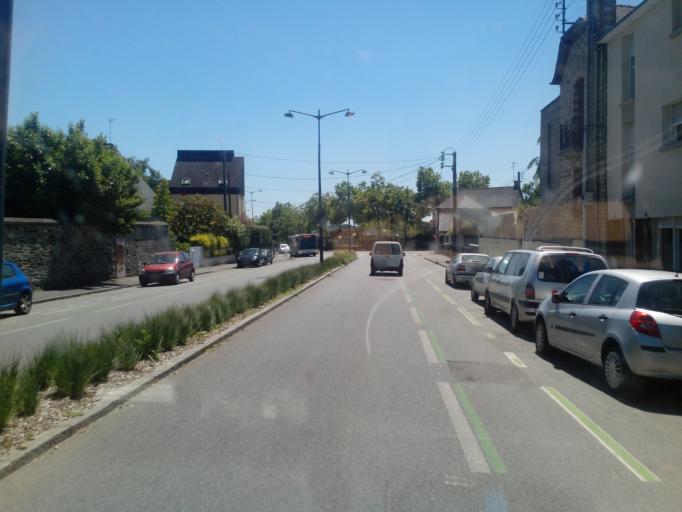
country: FR
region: Brittany
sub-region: Departement d'Ille-et-Vilaine
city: Rennes
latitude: 48.1151
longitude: -1.6483
